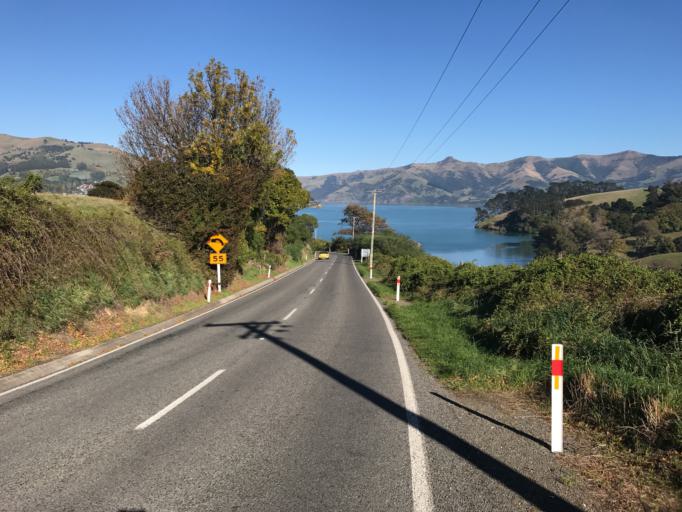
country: NZ
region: Canterbury
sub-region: Christchurch City
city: Christchurch
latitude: -43.7961
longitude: 172.9671
